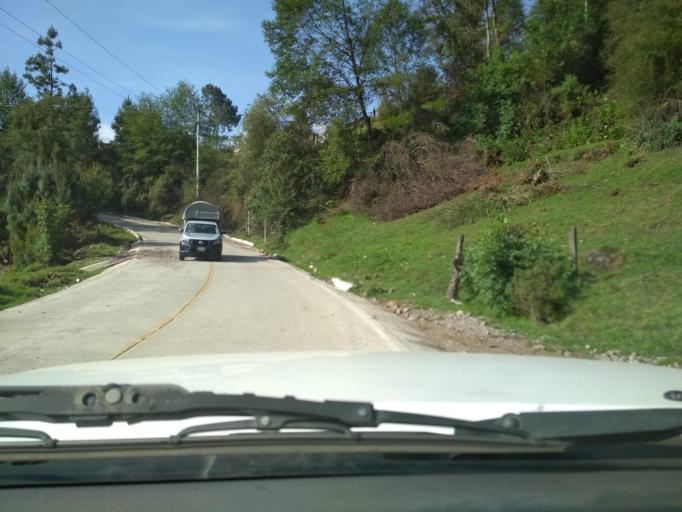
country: MX
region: Veracruz
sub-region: La Perla
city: Chilapa
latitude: 19.0044
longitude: -97.1826
